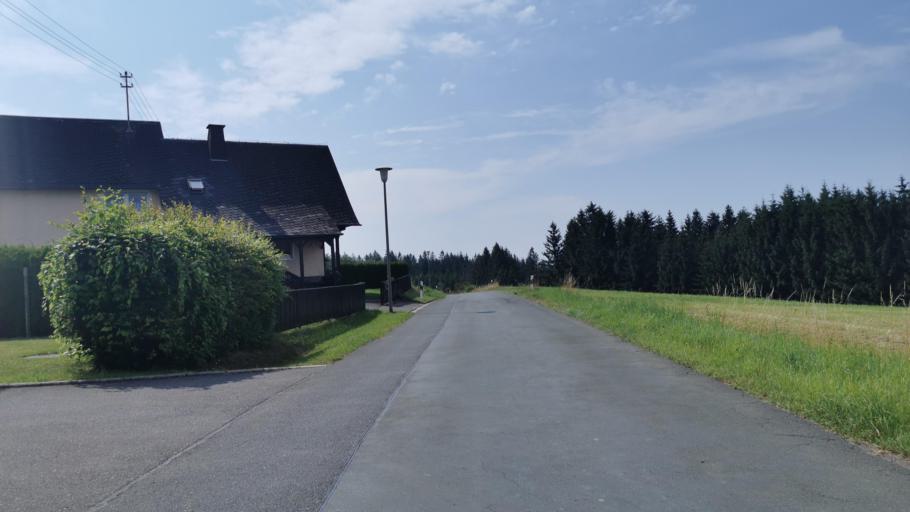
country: DE
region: Bavaria
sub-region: Upper Franconia
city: Wilhelmsthal
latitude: 50.2989
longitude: 11.3974
